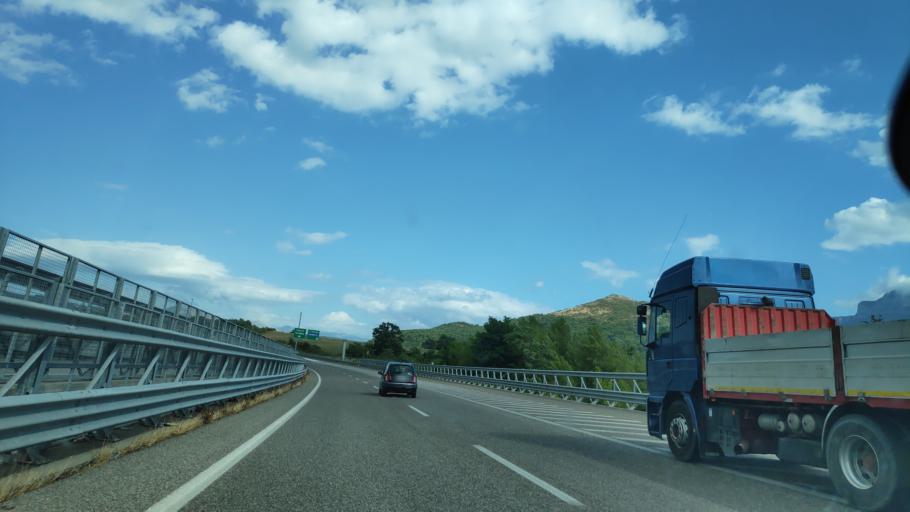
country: IT
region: Campania
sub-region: Provincia di Salerno
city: Palomonte
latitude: 40.6108
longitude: 15.2848
